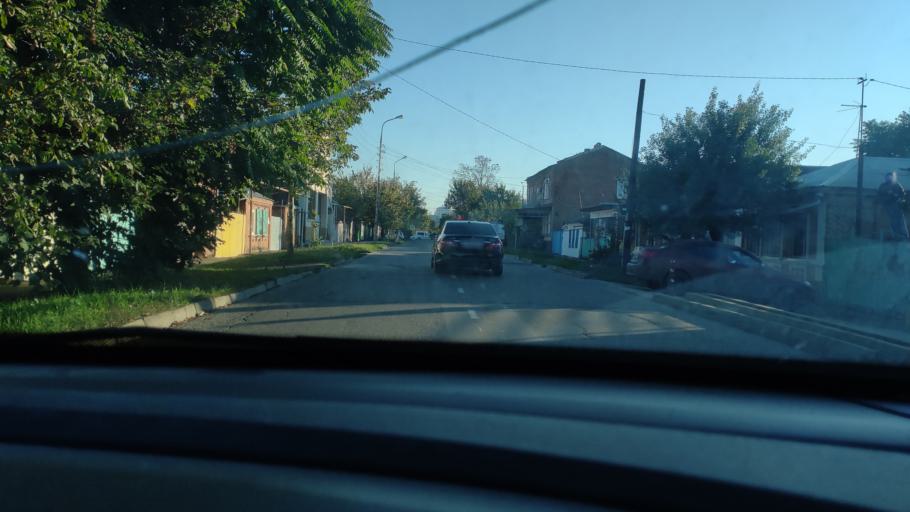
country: RU
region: Krasnodarskiy
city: Krasnodar
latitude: 45.0402
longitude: 38.9646
